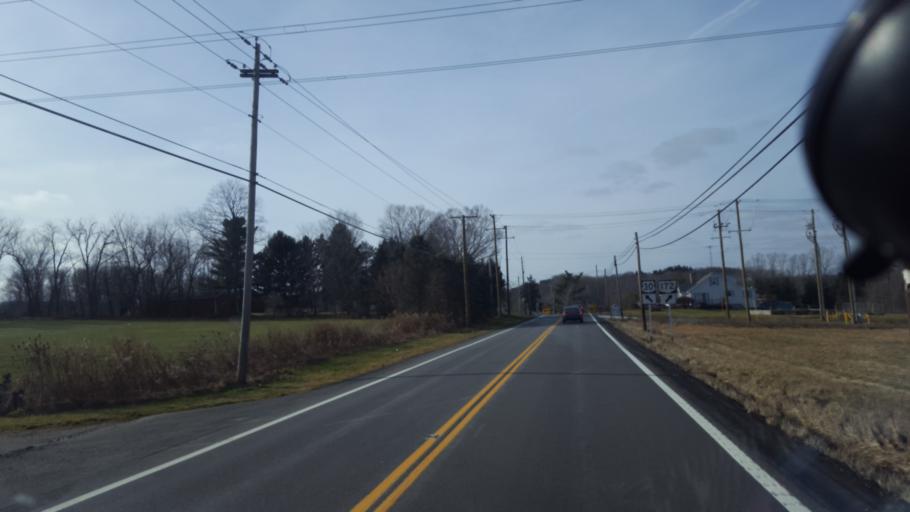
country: US
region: Ohio
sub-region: Columbiana County
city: Lisbon
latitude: 40.7700
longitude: -80.8025
